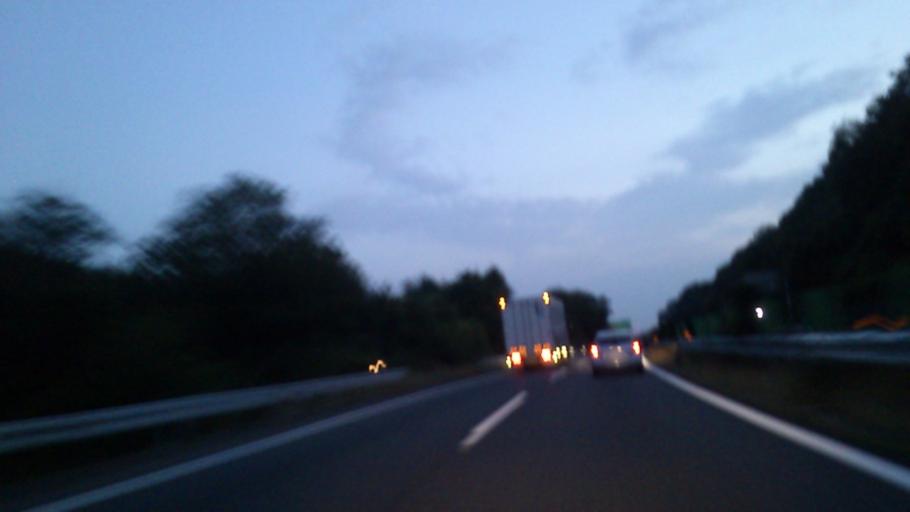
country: JP
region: Aichi
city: Kasugai
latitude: 35.3242
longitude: 137.0228
